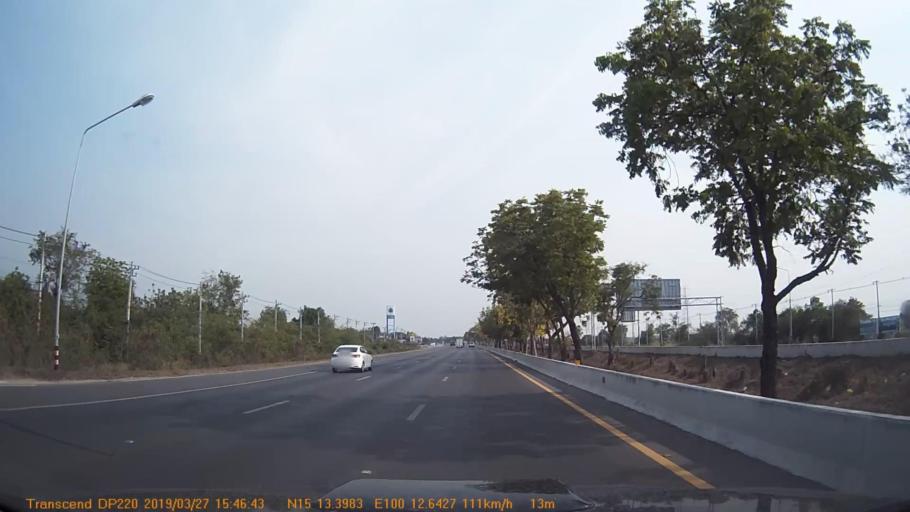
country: TH
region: Chai Nat
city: Sapphaya
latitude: 15.2227
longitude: 100.2109
